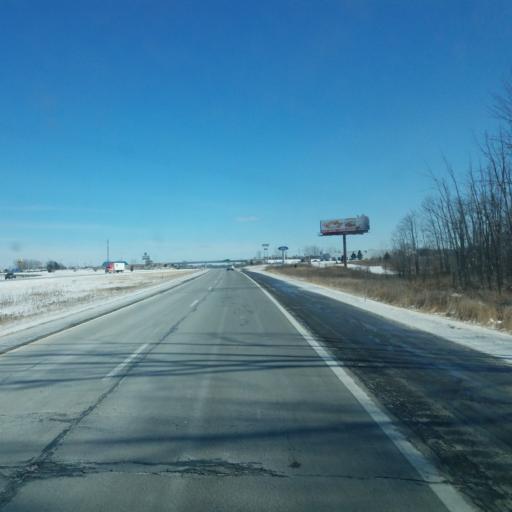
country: US
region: Michigan
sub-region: Livingston County
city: Fowlerville
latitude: 42.6460
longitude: -84.0781
